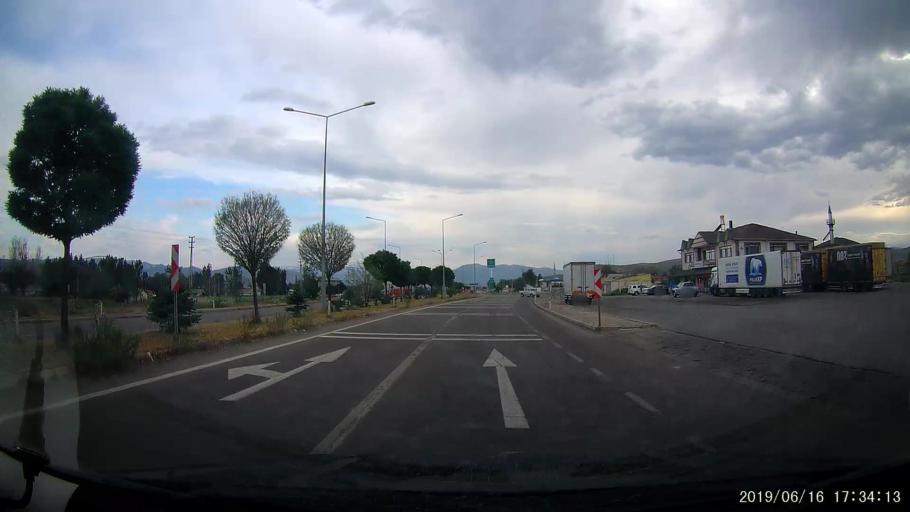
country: TR
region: Erzincan
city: Tercan
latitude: 39.7432
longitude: 40.2706
